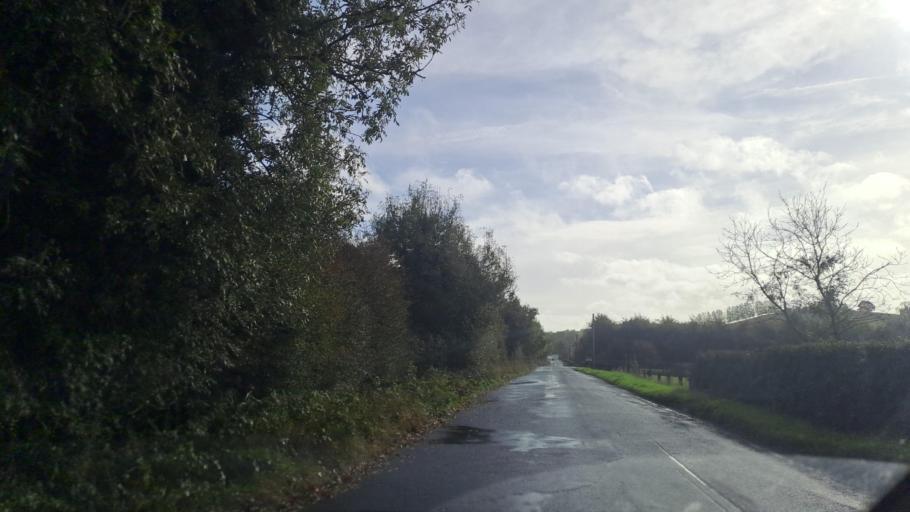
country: IE
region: Ulster
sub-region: County Monaghan
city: Carrickmacross
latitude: 53.8995
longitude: -6.6958
